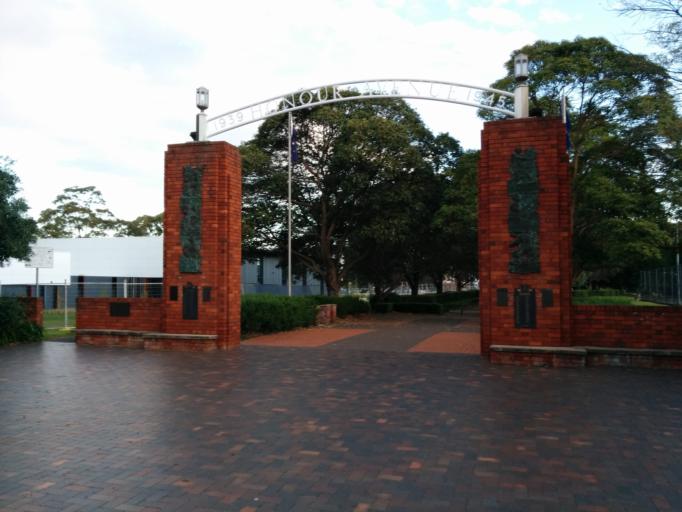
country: AU
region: New South Wales
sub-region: Fairfield
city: Carramar
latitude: -33.8743
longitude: 150.9595
